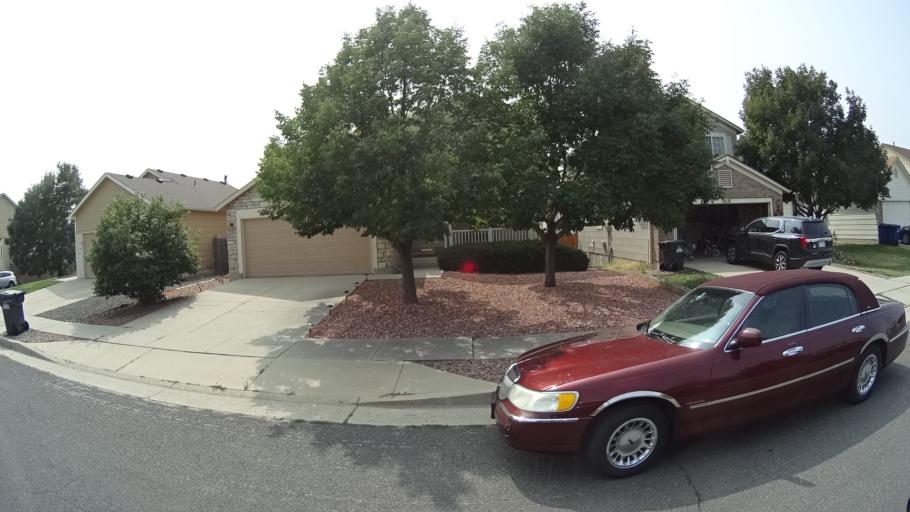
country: US
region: Colorado
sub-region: El Paso County
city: Cimarron Hills
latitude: 38.9243
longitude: -104.7253
